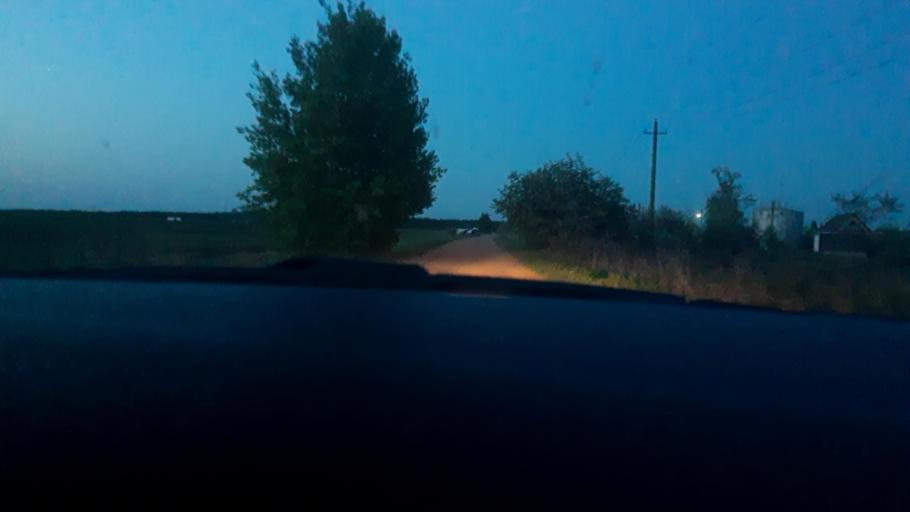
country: RU
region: Bashkortostan
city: Iglino
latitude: 54.7593
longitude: 56.3333
